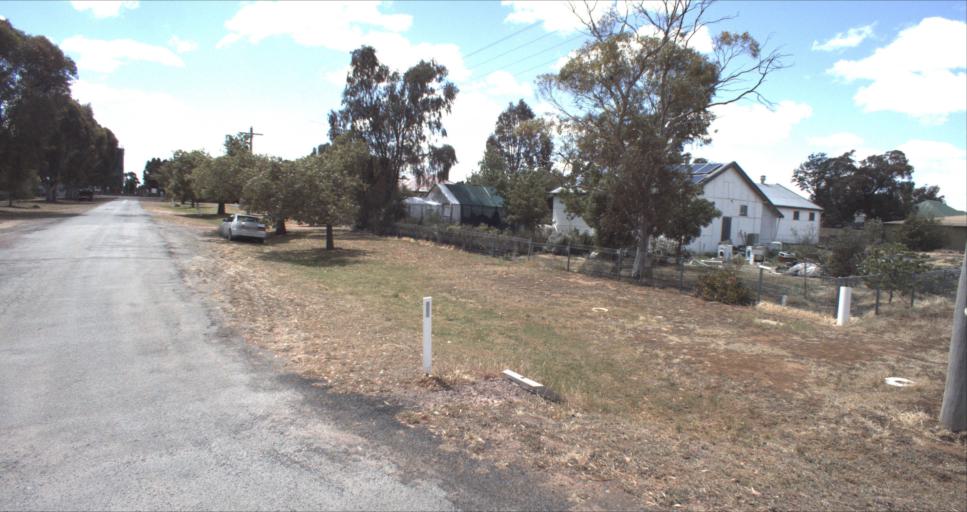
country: AU
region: New South Wales
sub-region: Murrumbidgee Shire
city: Darlington Point
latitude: -34.5196
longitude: 146.1817
